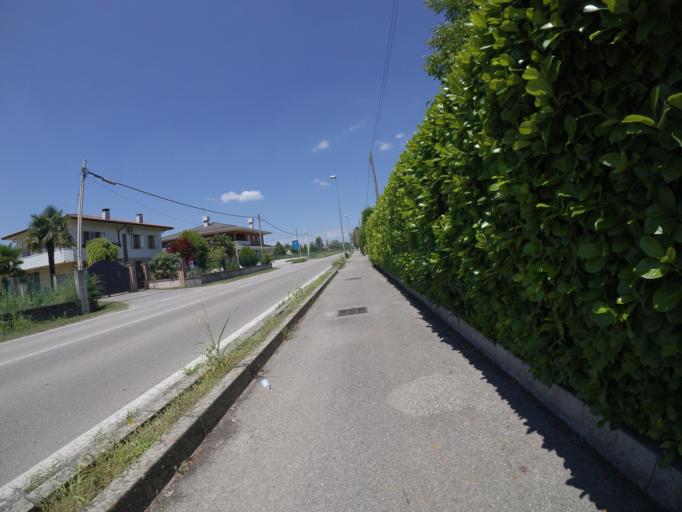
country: IT
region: Friuli Venezia Giulia
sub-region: Provincia di Udine
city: Rivignano
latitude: 45.8840
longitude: 13.0376
